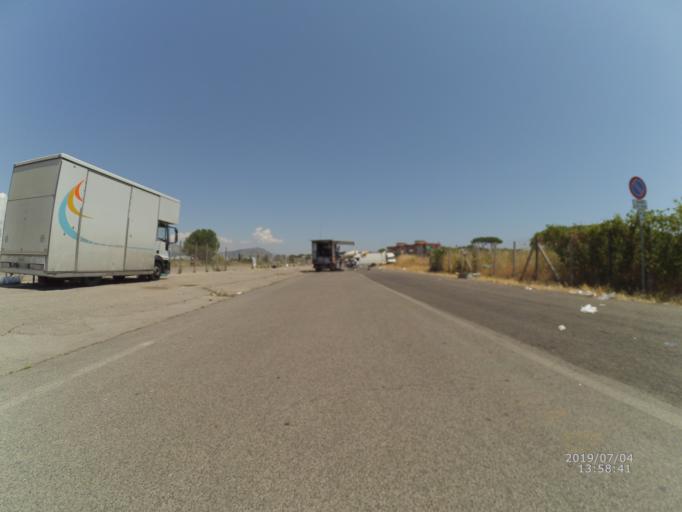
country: IT
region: Latium
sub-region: Provincia di Latina
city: Terracina
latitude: 41.2874
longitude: 13.2097
